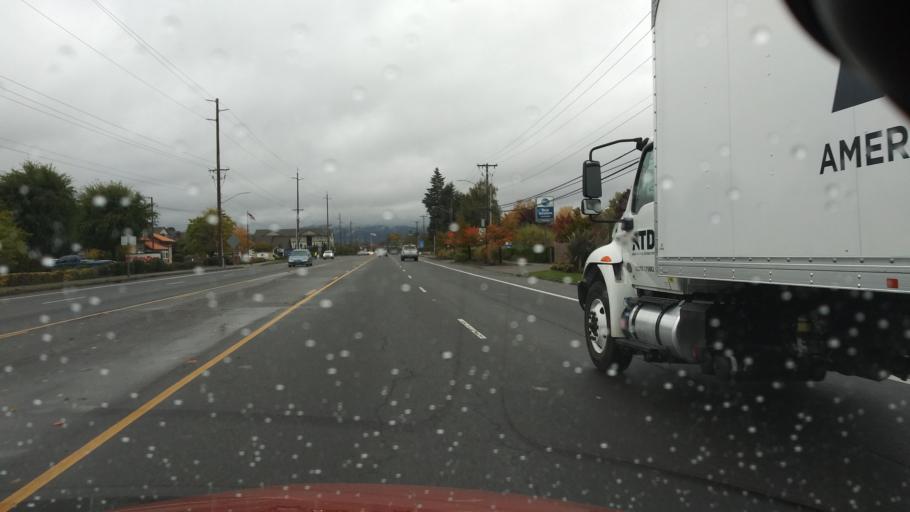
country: US
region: Oregon
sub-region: Washington County
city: Cornelius
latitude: 45.5203
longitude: -123.0764
